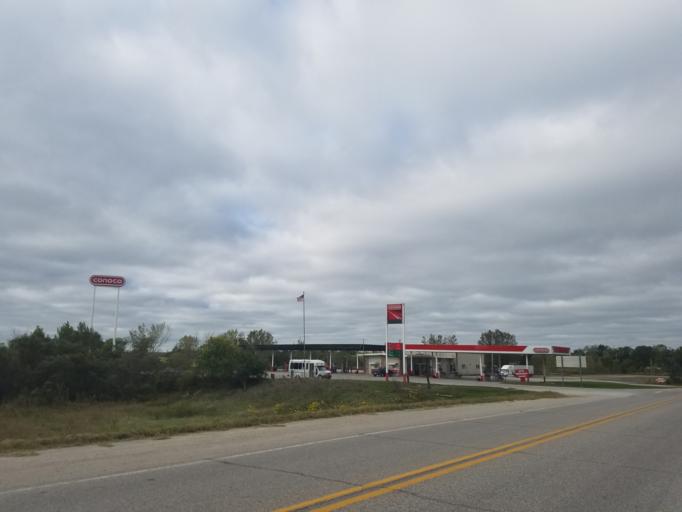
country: US
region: Iowa
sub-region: Decatur County
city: Lamoni
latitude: 40.5751
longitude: -93.9408
